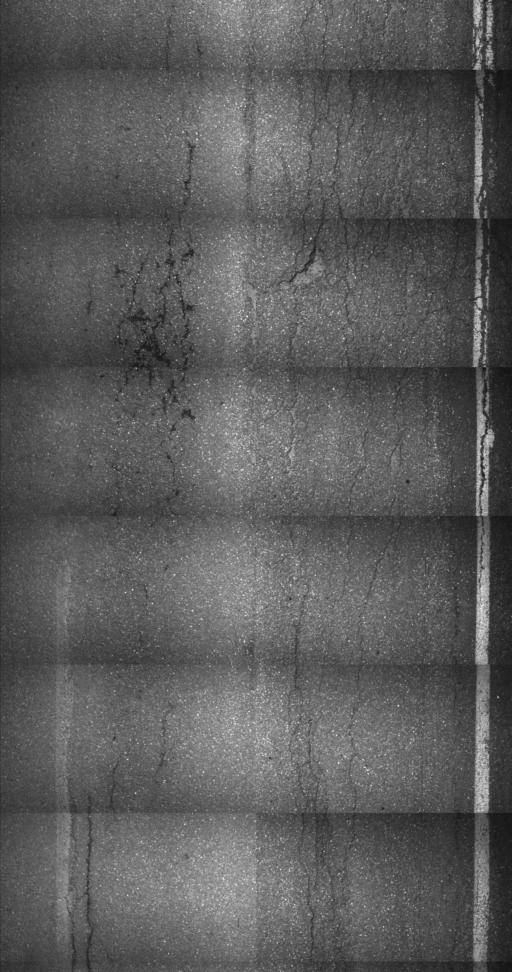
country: US
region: New York
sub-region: Essex County
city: Ticonderoga
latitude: 43.8624
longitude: -73.3503
